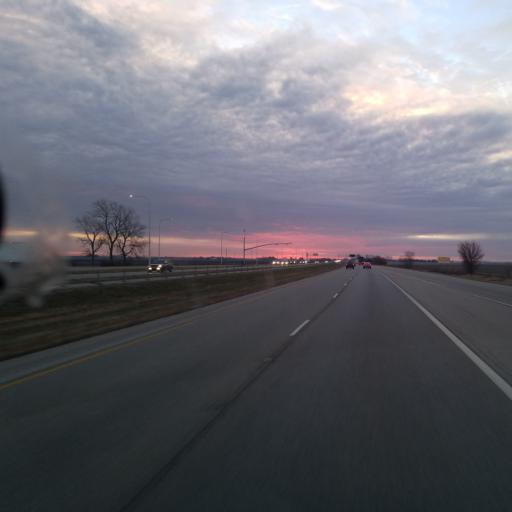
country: US
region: Illinois
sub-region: McLean County
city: Twin Grove
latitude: 40.5557
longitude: -89.1039
